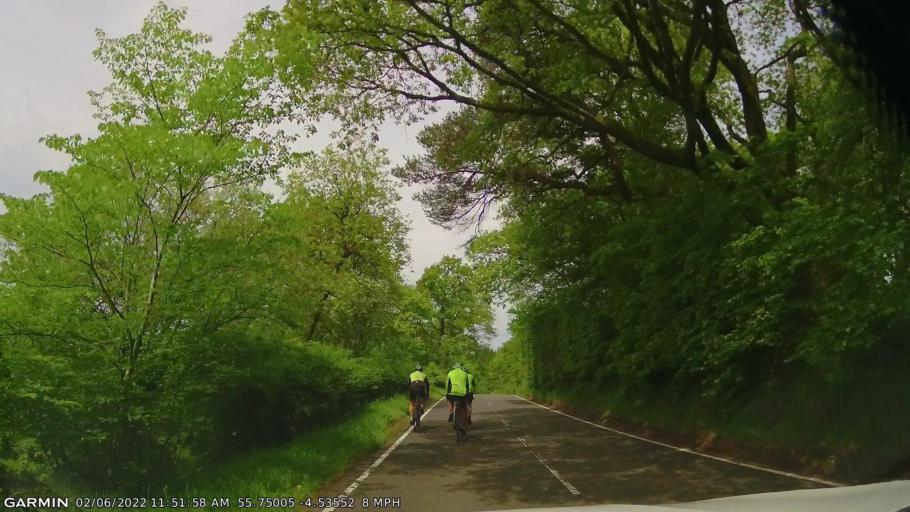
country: GB
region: Scotland
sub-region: Renfrewshire
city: Howwood
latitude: 55.7501
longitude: -4.5355
